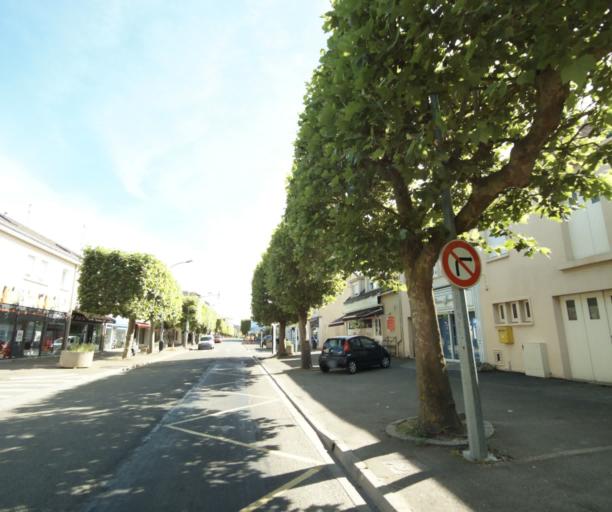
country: FR
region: Centre
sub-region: Departement d'Eure-et-Loir
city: Luisant
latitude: 48.4373
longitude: 1.4722
